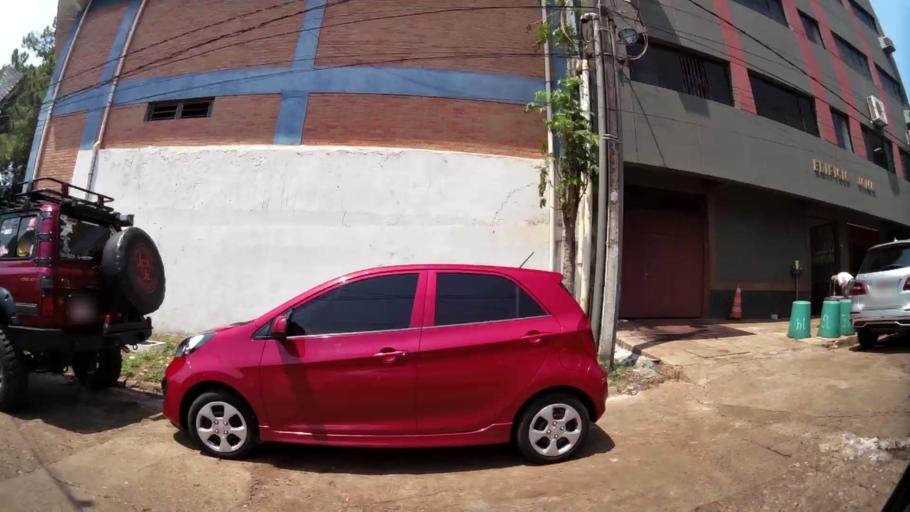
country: PY
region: Alto Parana
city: Ciudad del Este
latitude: -25.5141
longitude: -54.6082
